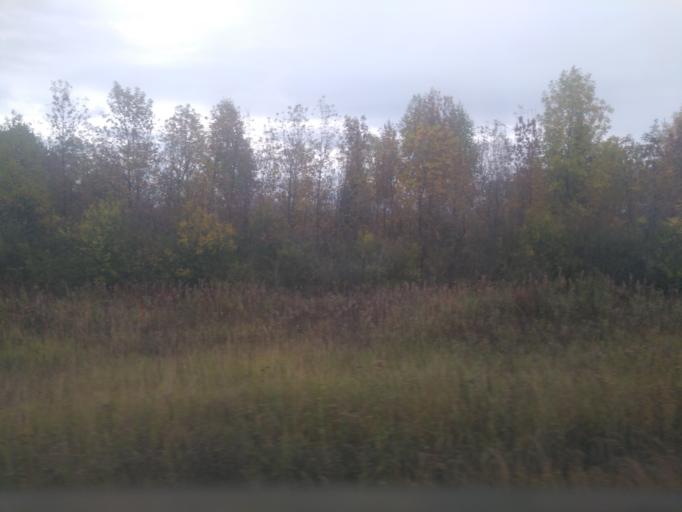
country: RU
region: Udmurtiya
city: Alnashi
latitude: 56.2093
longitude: 52.6241
